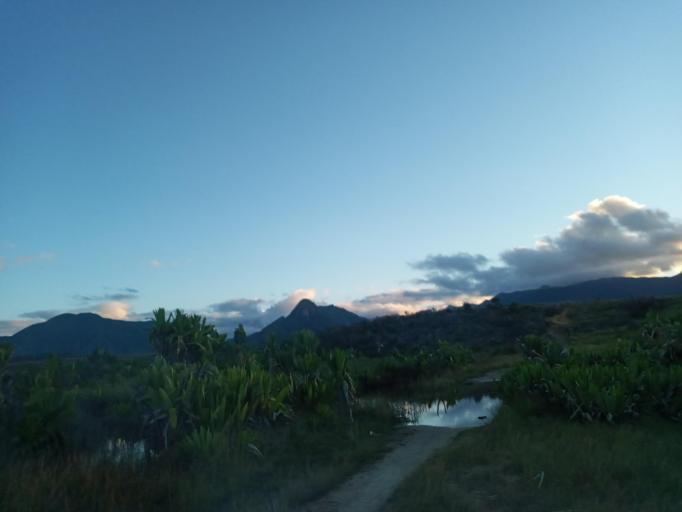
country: MG
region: Anosy
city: Fort Dauphin
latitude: -24.5130
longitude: 47.2367
